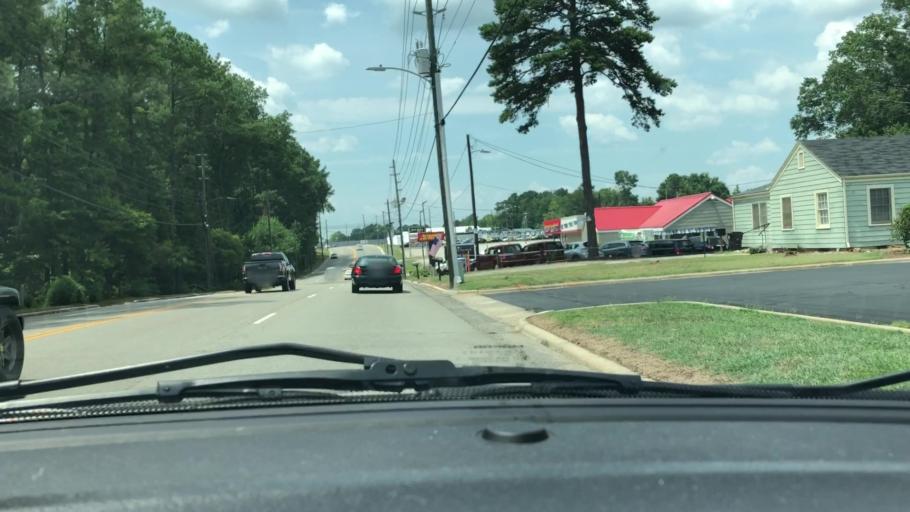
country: US
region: North Carolina
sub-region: Lee County
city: Sanford
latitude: 35.4897
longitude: -79.1887
